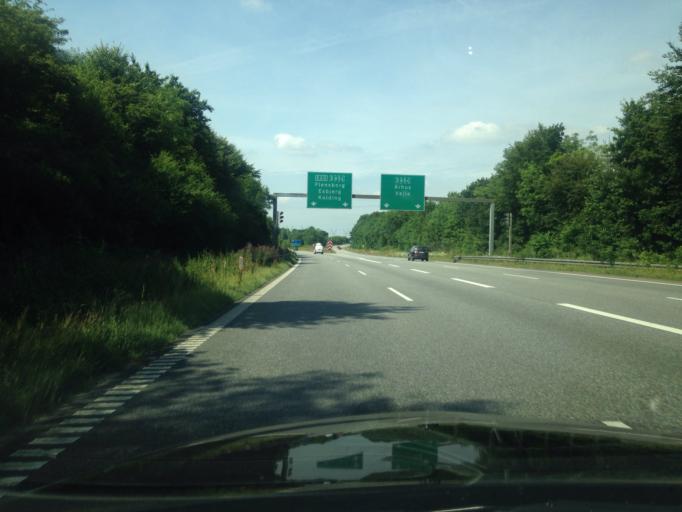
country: DK
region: South Denmark
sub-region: Fredericia Kommune
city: Taulov
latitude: 55.5400
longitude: 9.6675
